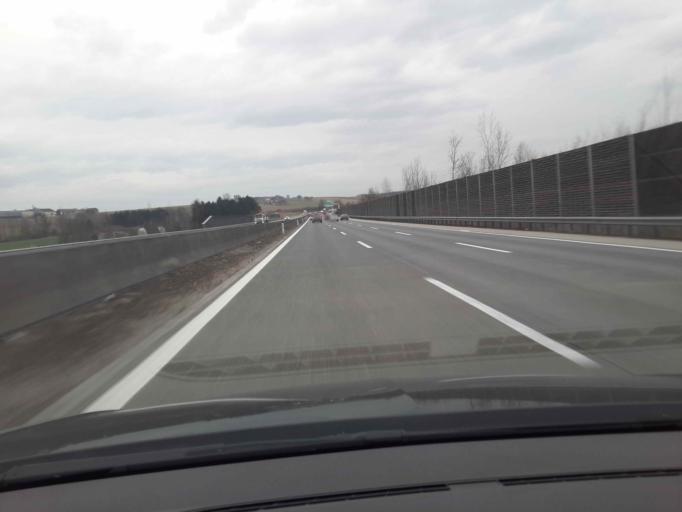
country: AT
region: Lower Austria
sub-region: Politischer Bezirk Melk
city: Erlauf
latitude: 48.1673
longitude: 15.1679
